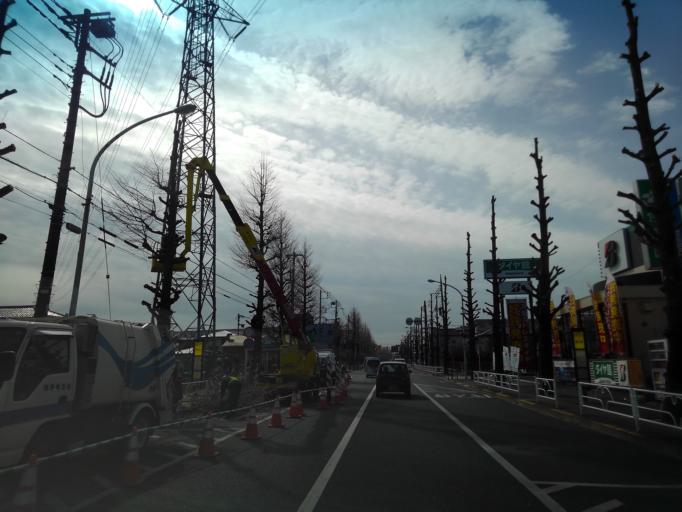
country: JP
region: Tokyo
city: Tanashicho
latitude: 35.7500
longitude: 139.5052
